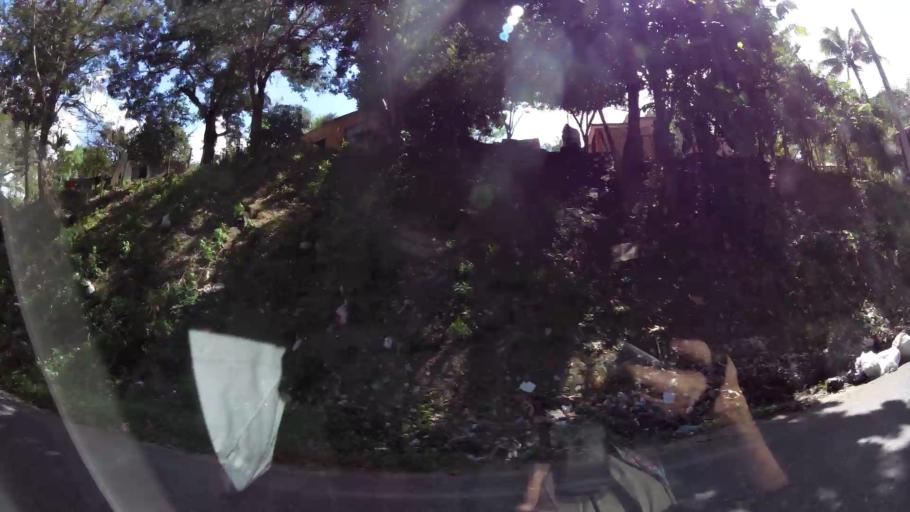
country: DO
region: San Cristobal
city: San Cristobal
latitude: 18.4290
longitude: -70.0857
